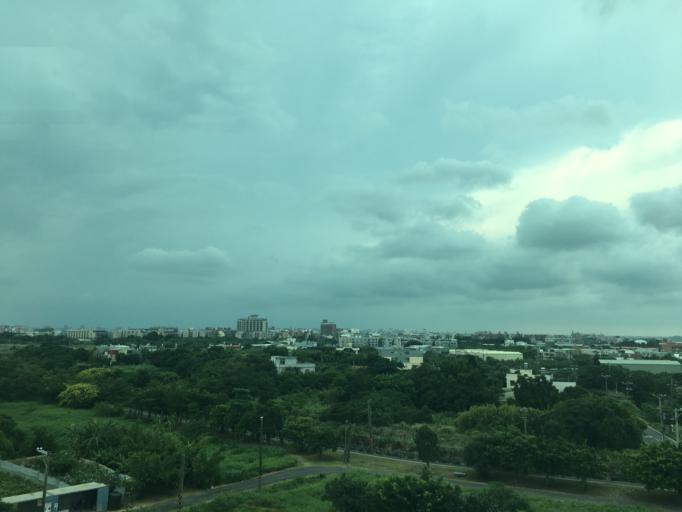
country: TW
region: Taiwan
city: Taoyuan City
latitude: 25.0872
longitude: 121.2649
